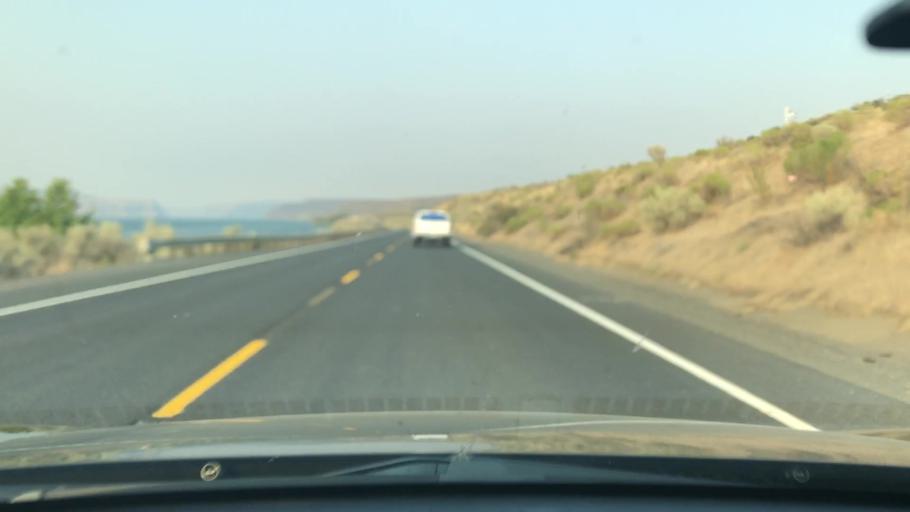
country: US
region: Oregon
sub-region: Umatilla County
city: Stanfield
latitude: 45.9220
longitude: -119.1179
